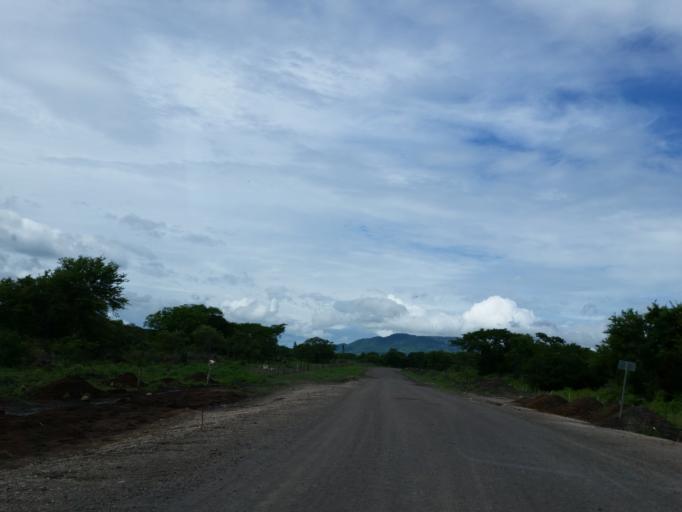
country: NI
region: Leon
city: Larreynaga
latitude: 12.5877
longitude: -86.6403
